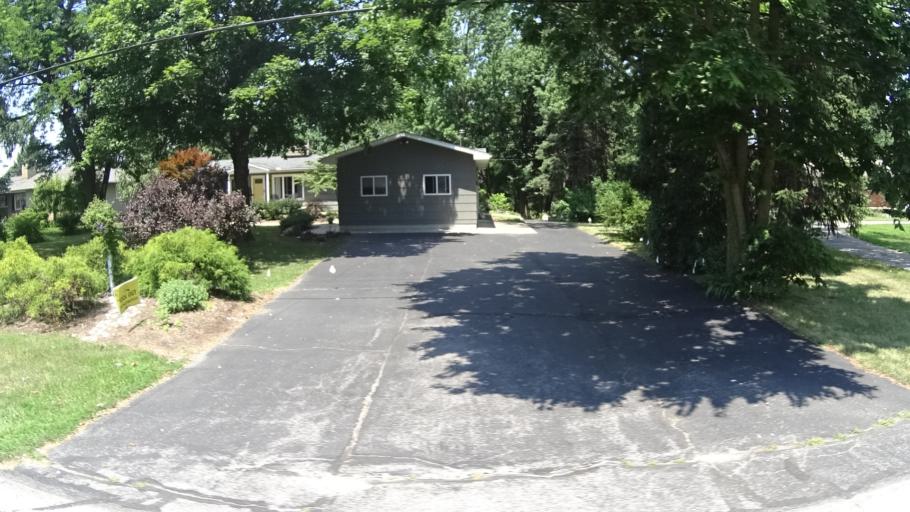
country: US
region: Ohio
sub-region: Erie County
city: Huron
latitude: 41.4130
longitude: -82.6225
